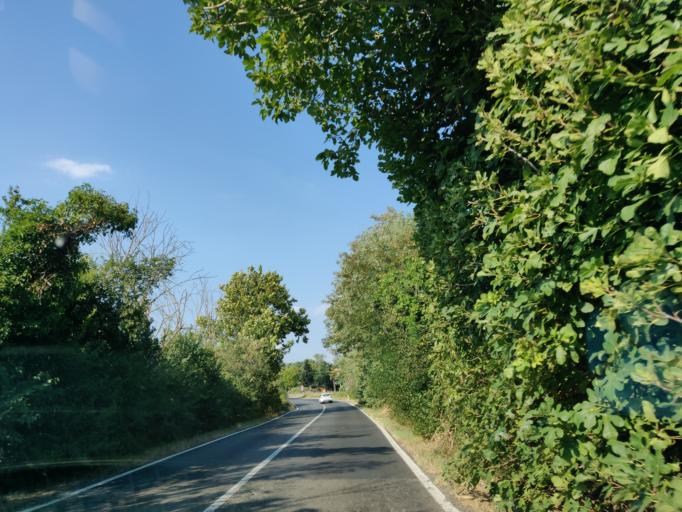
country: IT
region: Latium
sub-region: Provincia di Viterbo
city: Canino
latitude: 42.4115
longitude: 11.6995
